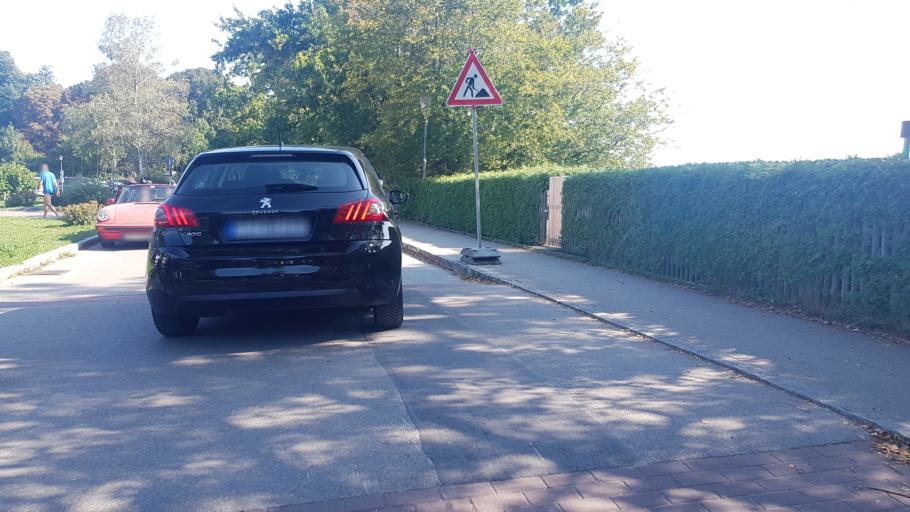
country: DE
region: Bavaria
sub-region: Upper Bavaria
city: Worthsee
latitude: 48.0729
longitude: 11.1960
